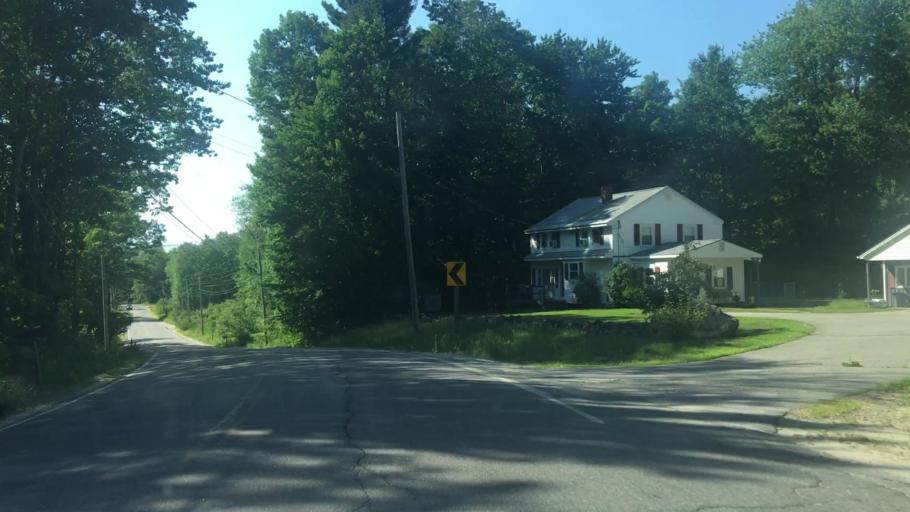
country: US
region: Maine
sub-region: York County
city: Hollis Center
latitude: 43.6451
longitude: -70.5854
